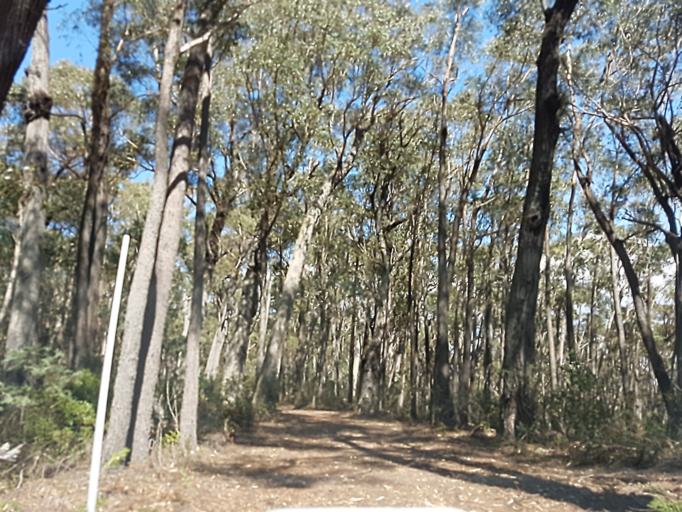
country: AU
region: Victoria
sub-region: East Gippsland
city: Lakes Entrance
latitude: -37.2899
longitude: 148.3232
